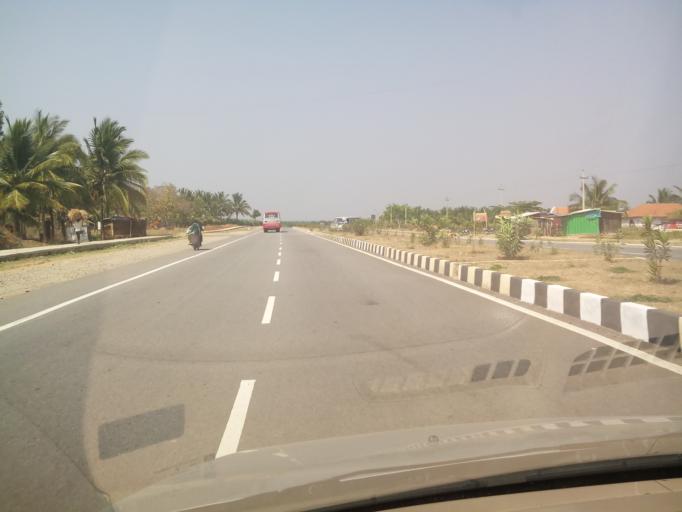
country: IN
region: Karnataka
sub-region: Hassan
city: Shravanabelagola
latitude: 12.9186
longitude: 76.4677
